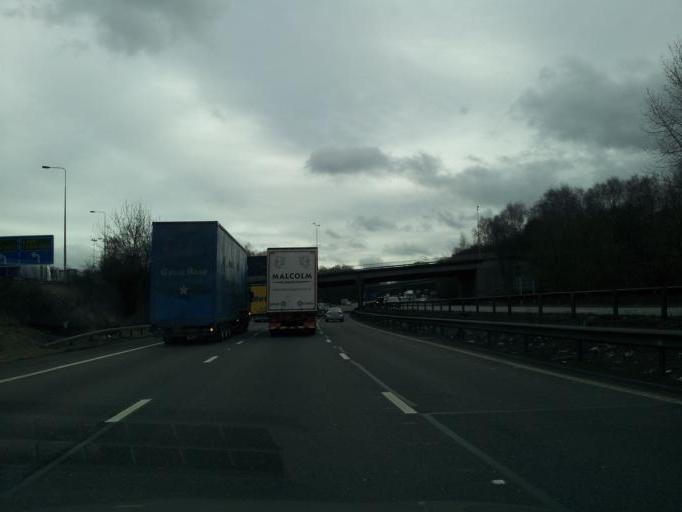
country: GB
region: England
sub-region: Staffordshire
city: Newcastle under Lyme
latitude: 52.9769
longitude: -2.2272
